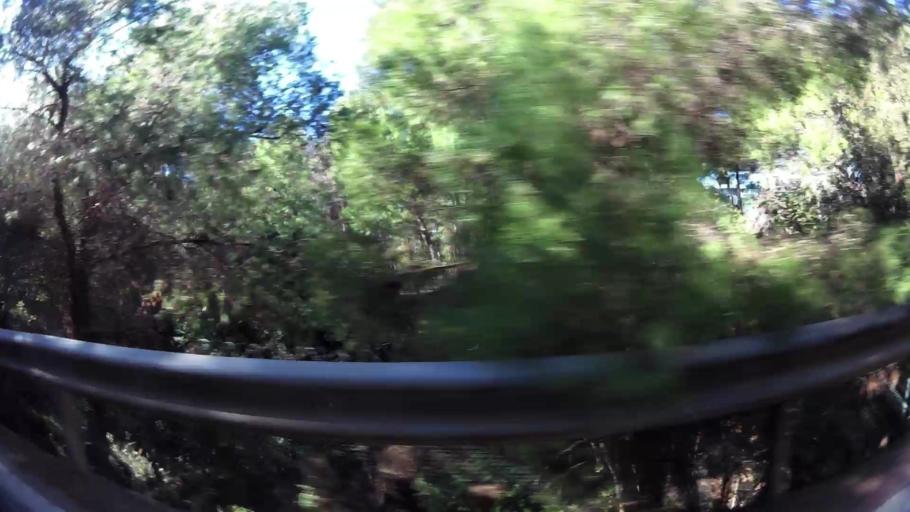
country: GR
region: Attica
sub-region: Nomarchia Anatolikis Attikis
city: Varybobi
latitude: 38.1183
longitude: 23.7991
